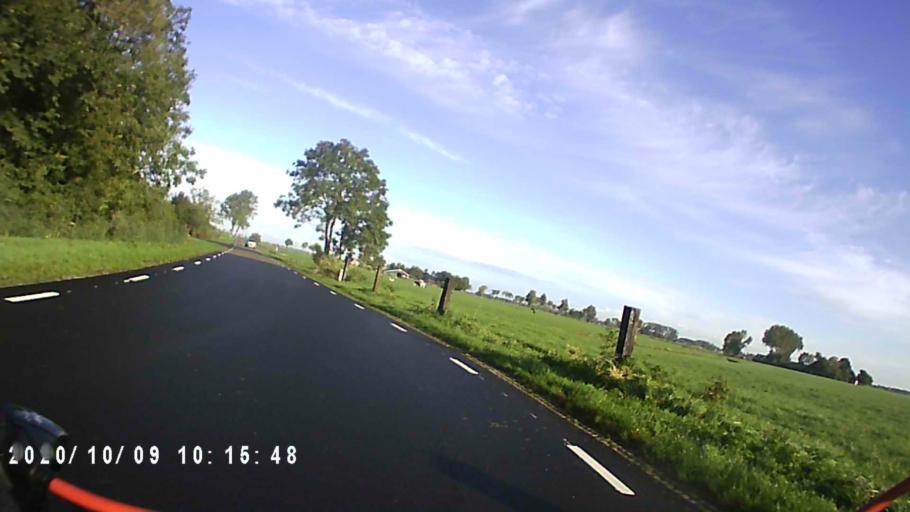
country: NL
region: Groningen
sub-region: Gemeente Winsum
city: Winsum
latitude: 53.3073
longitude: 6.5042
